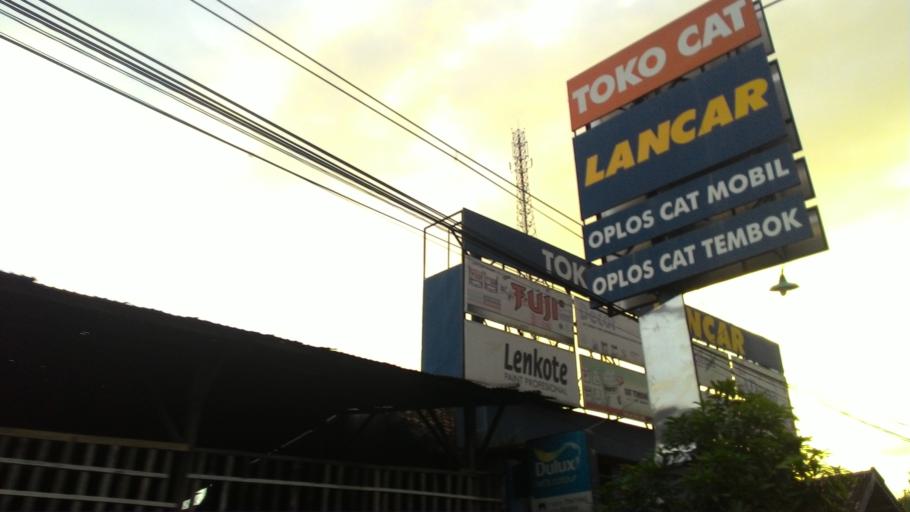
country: ID
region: Daerah Istimewa Yogyakarta
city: Depok
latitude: -7.8276
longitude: 110.4397
